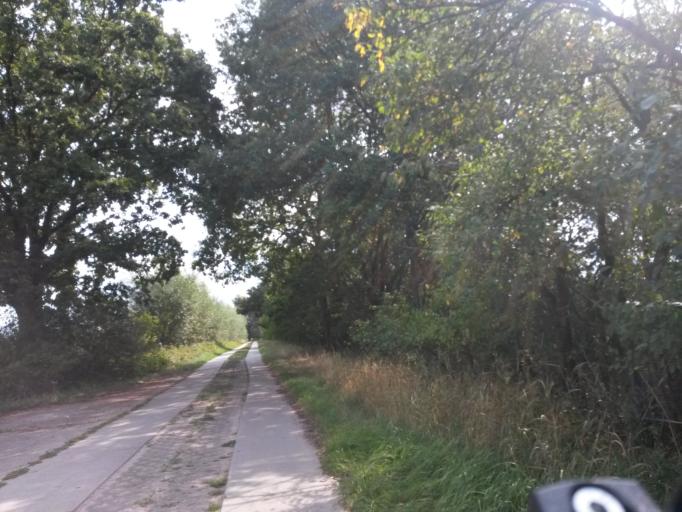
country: DE
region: Saxony-Anhalt
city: Arneburg
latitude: 52.6471
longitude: 12.0350
